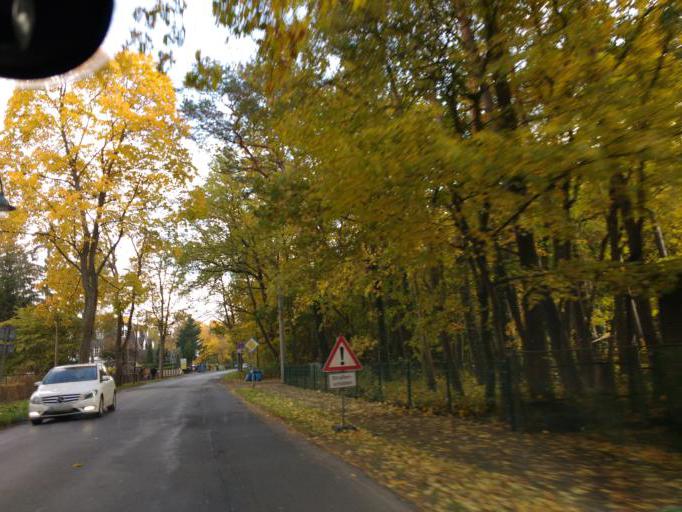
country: DE
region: Brandenburg
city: Petershagen
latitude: 52.5558
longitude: 13.8316
